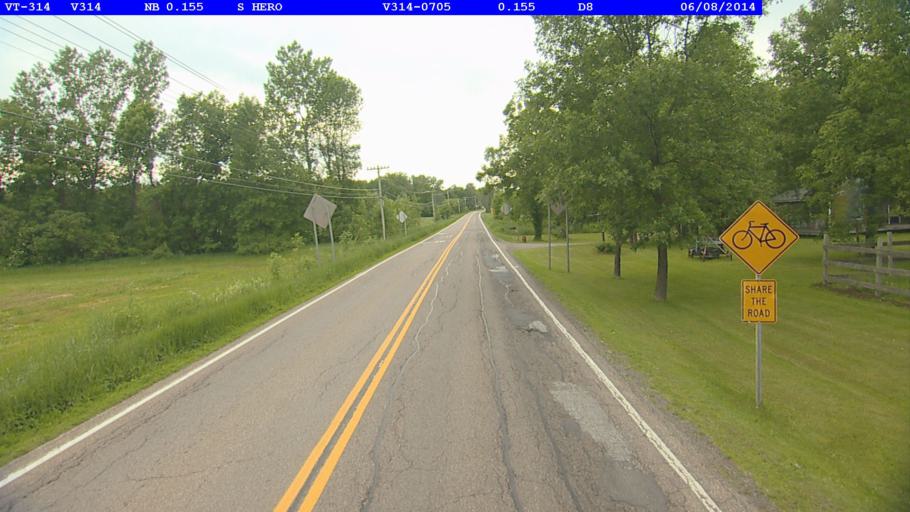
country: US
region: New York
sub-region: Clinton County
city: Cumberland Head
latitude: 44.6652
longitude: -73.3256
